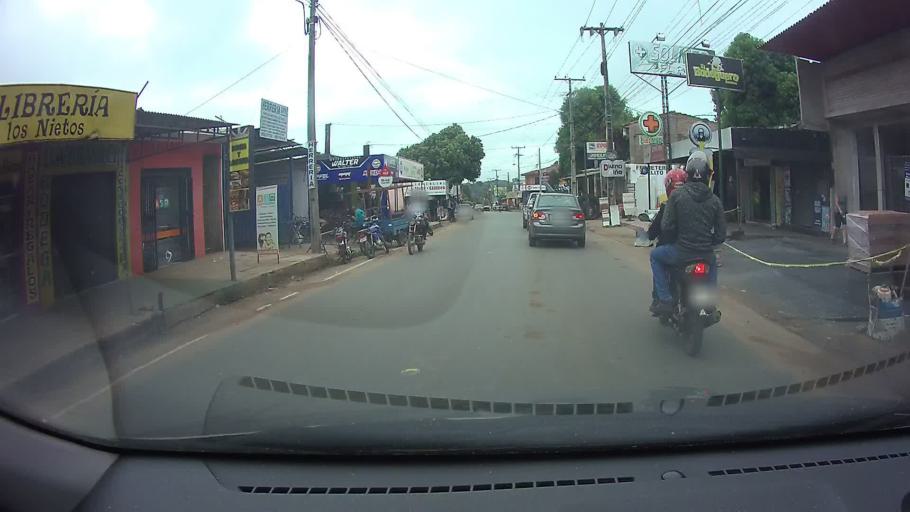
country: PY
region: Central
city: San Lorenzo
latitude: -25.3189
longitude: -57.4957
